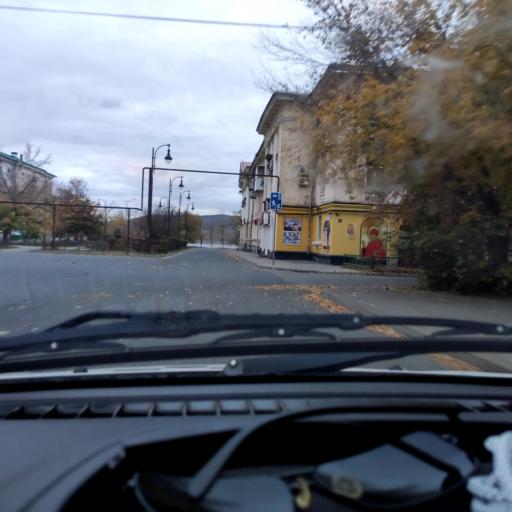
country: RU
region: Samara
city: Zhigulevsk
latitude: 53.4654
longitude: 49.5320
